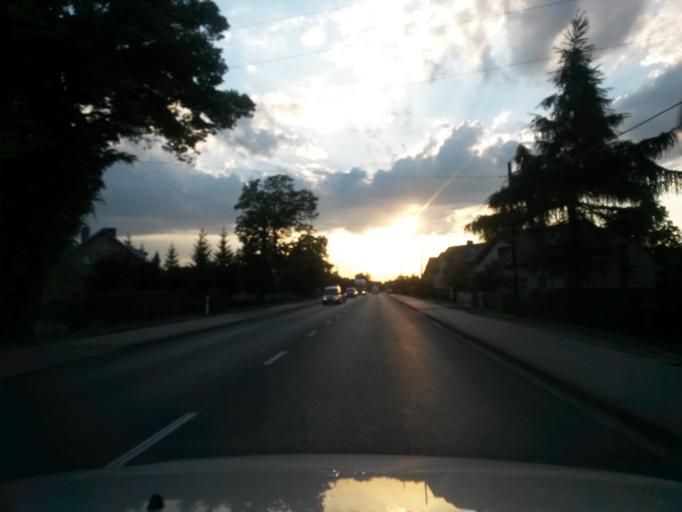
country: PL
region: Lodz Voivodeship
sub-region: Powiat wielunski
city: Wielun
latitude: 51.2300
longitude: 18.5457
